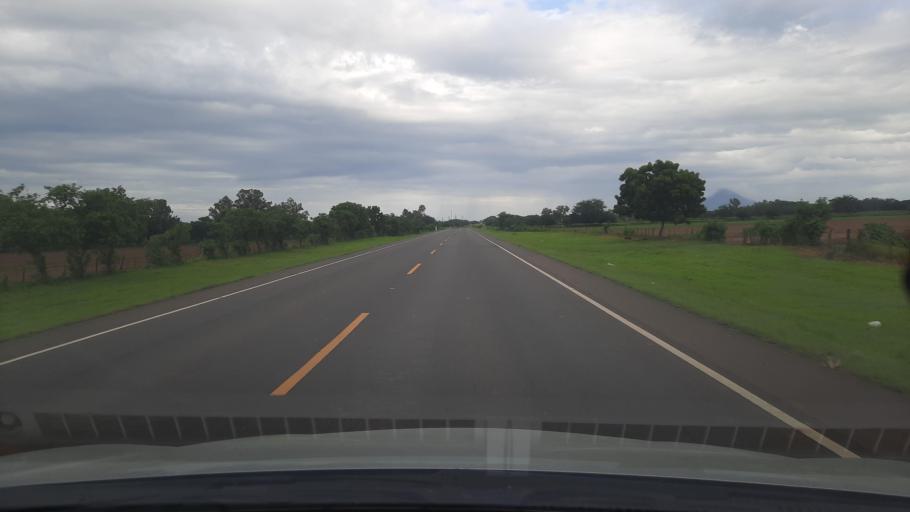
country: NI
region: Leon
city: Larreynaga
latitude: 12.6145
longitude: -86.6825
